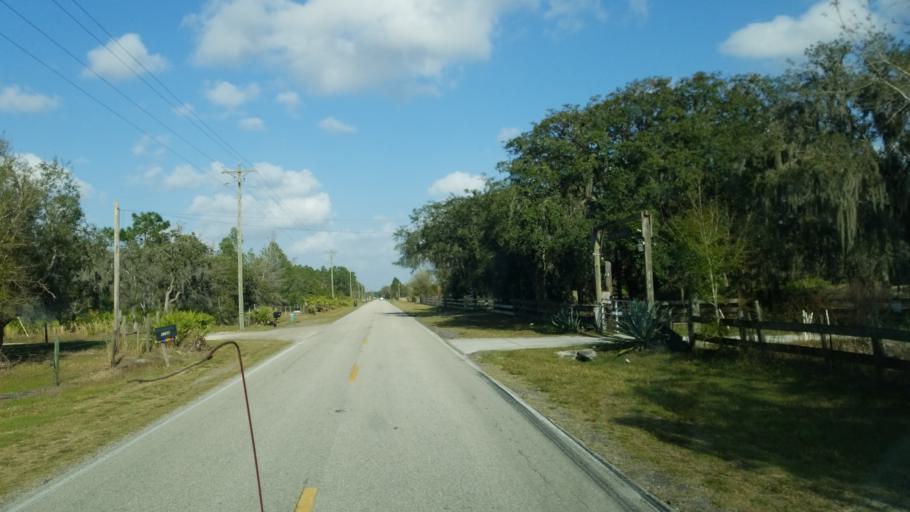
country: US
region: Florida
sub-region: Hardee County
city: Wauchula
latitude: 27.4473
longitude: -82.1104
